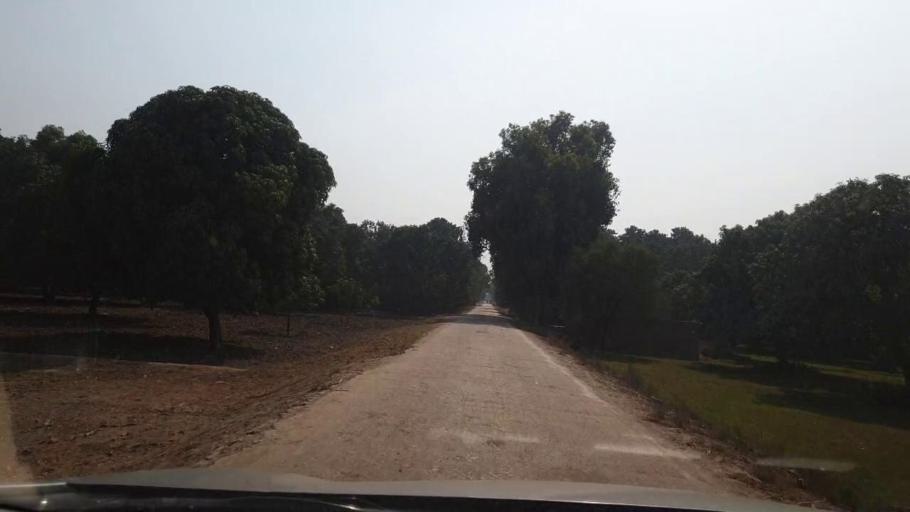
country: PK
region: Sindh
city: Tando Allahyar
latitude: 25.4822
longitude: 68.7714
